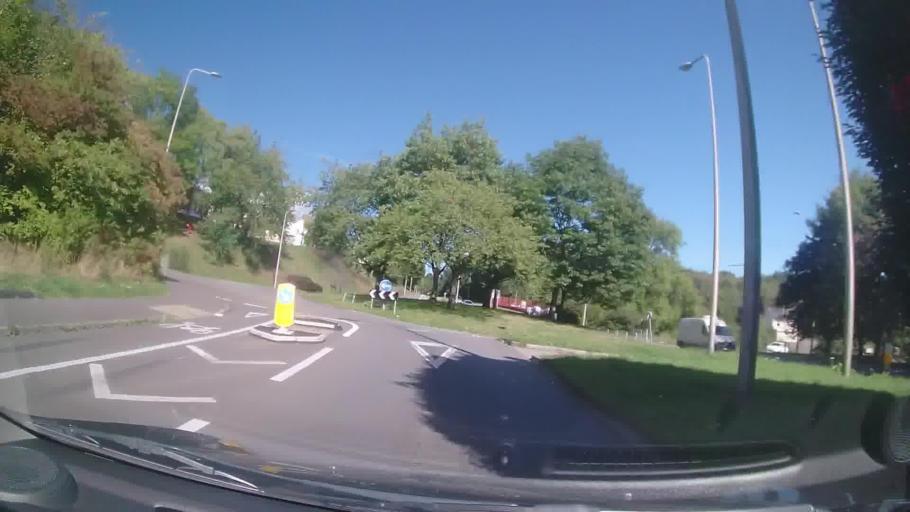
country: GB
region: Wales
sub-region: Merthyr Tydfil County Borough
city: Merthyr Tydfil
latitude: 51.7537
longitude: -3.3707
